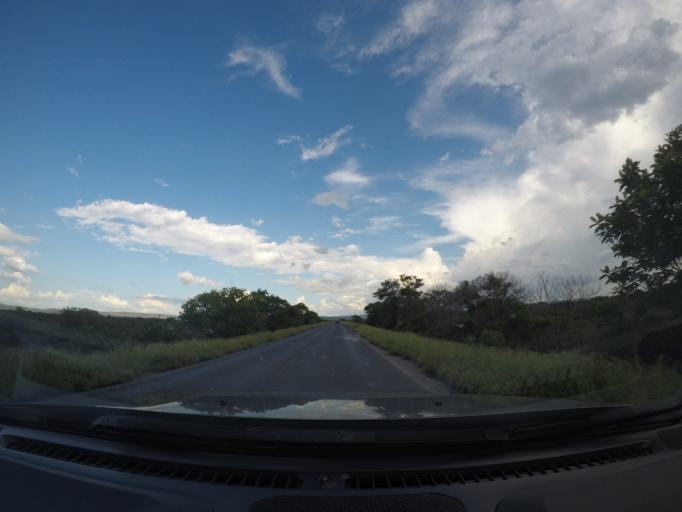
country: BR
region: Bahia
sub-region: Ibotirama
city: Ibotirama
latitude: -12.1659
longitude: -43.2773
